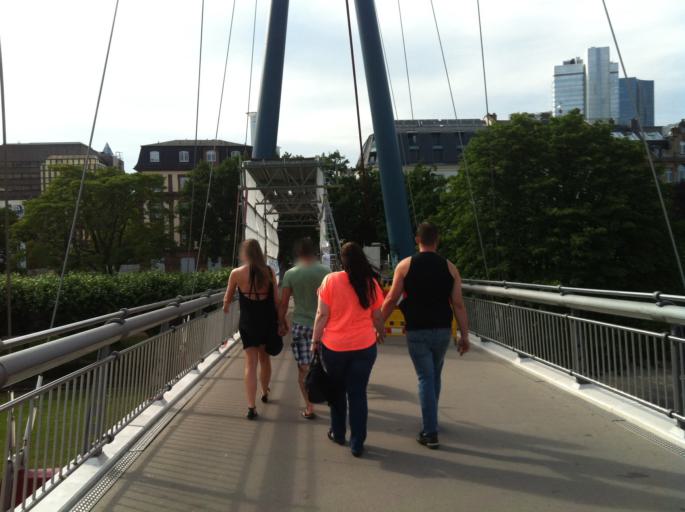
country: DE
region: Hesse
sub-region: Regierungsbezirk Darmstadt
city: Frankfurt am Main
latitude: 50.1043
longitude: 8.6715
